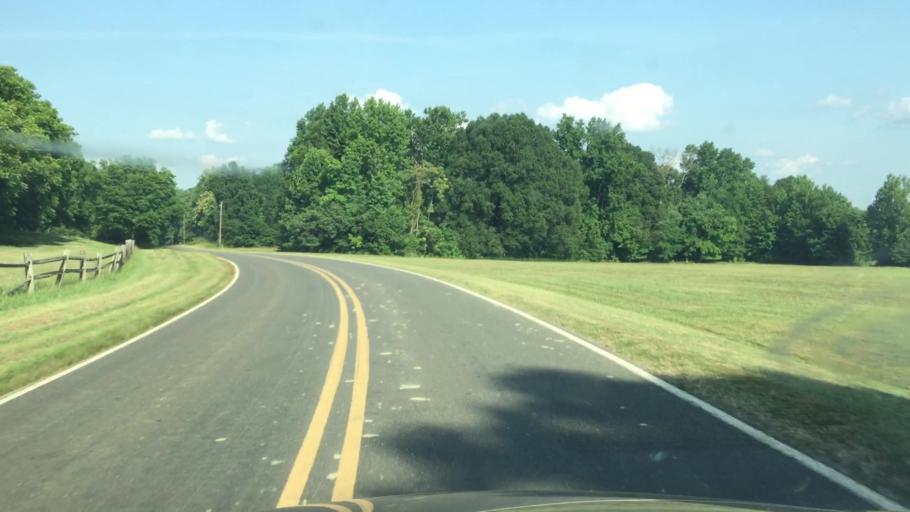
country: US
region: North Carolina
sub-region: Rockingham County
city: Reidsville
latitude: 36.2753
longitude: -79.5857
